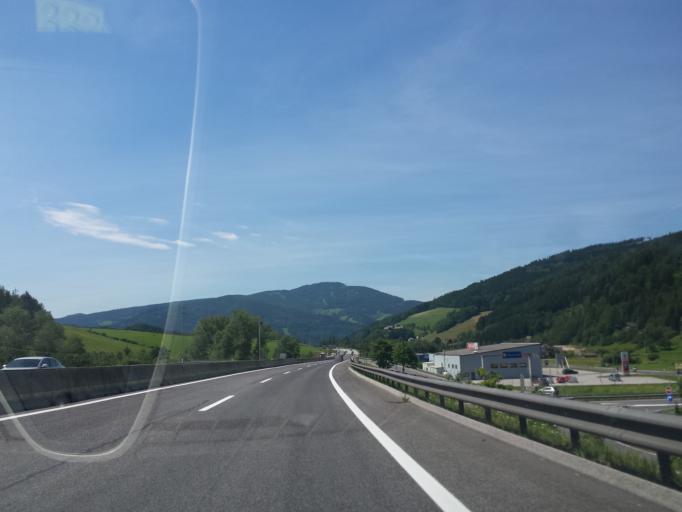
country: AT
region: Styria
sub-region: Politischer Bezirk Bruck-Muerzzuschlag
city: Spital am Semmering
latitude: 47.6011
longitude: 15.7220
